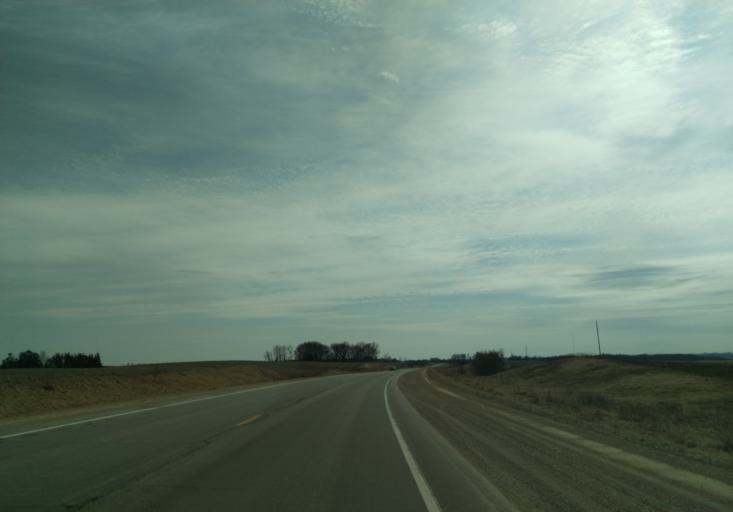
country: US
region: Iowa
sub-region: Winneshiek County
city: Decorah
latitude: 43.3633
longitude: -91.8043
